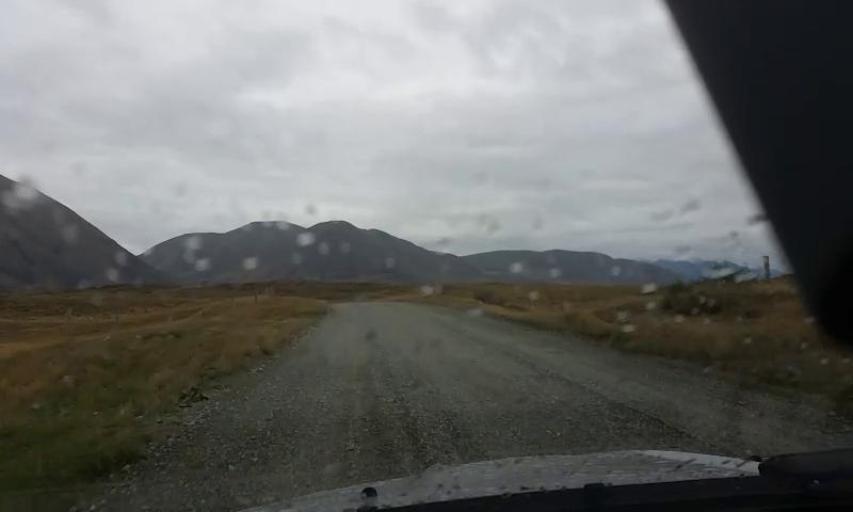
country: NZ
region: Canterbury
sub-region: Ashburton District
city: Methven
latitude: -43.6152
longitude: 171.1030
